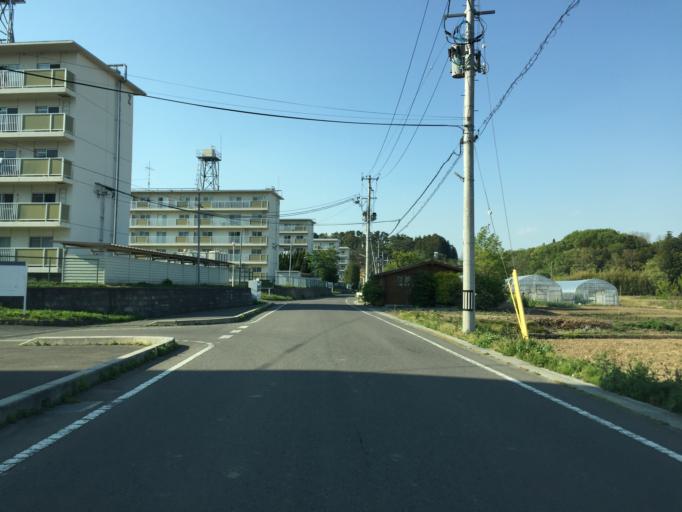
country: JP
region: Fukushima
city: Koriyama
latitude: 37.4044
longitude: 140.3215
